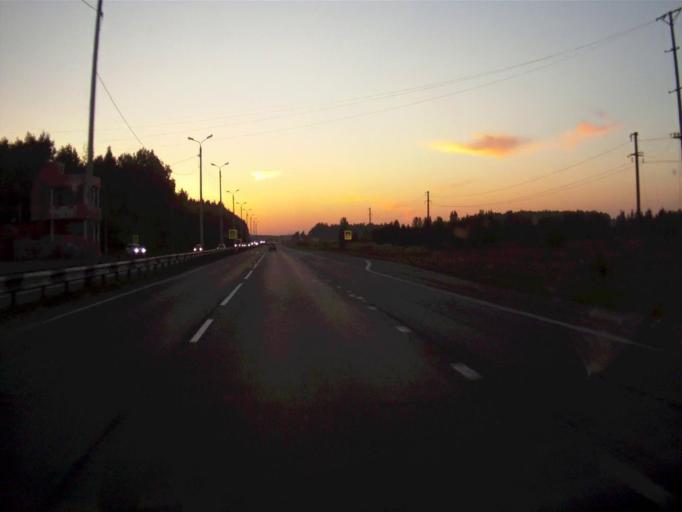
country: RU
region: Chelyabinsk
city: Roshchino
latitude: 55.1905
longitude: 61.2283
